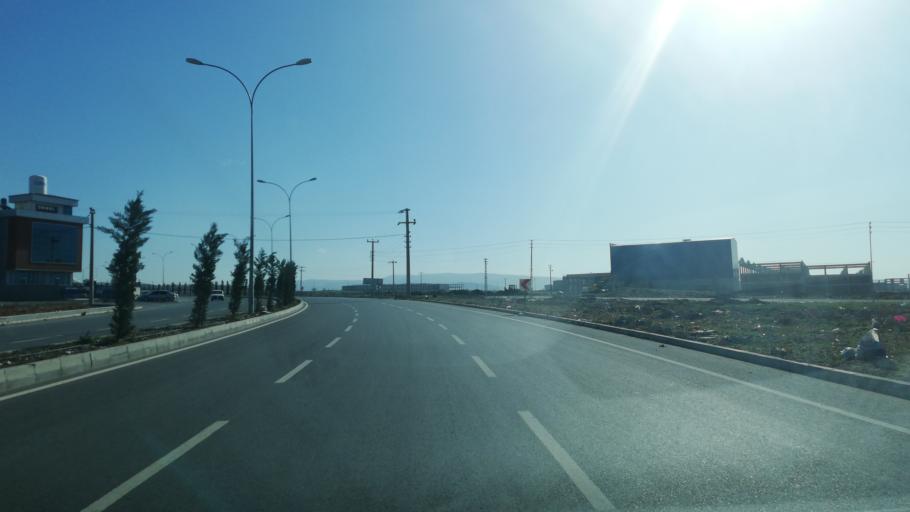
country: TR
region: Kahramanmaras
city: Kahramanmaras
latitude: 37.5709
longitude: 36.9688
